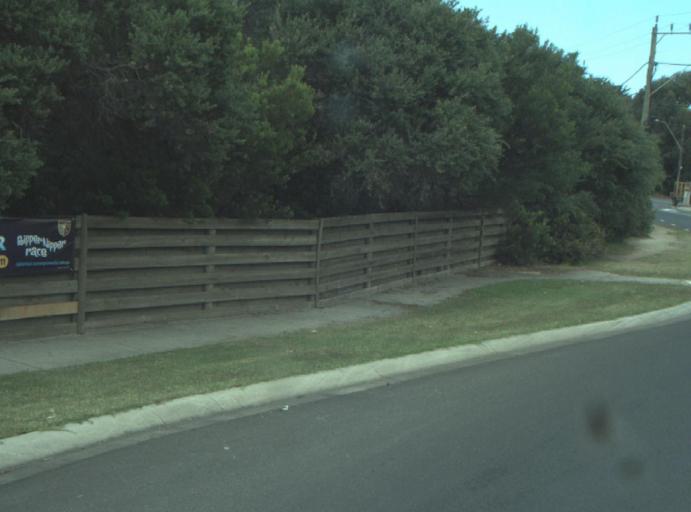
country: AU
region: Victoria
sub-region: Greater Geelong
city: Leopold
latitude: -38.2687
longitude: 144.5147
